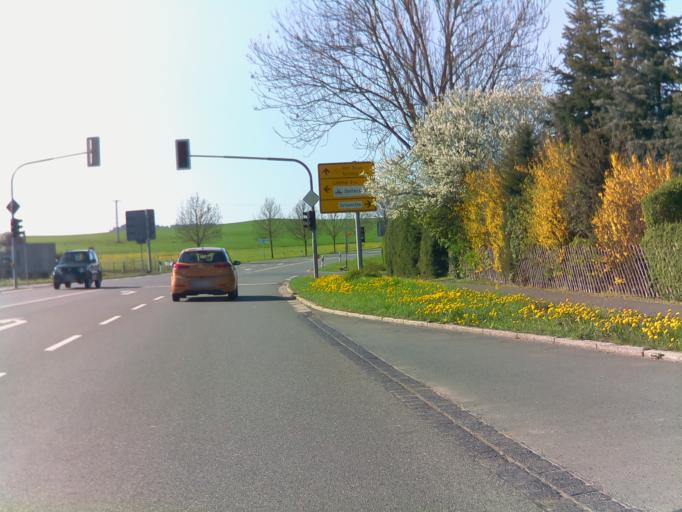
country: DE
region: Thuringia
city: Oettersdorf
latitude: 50.6020
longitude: 11.8246
